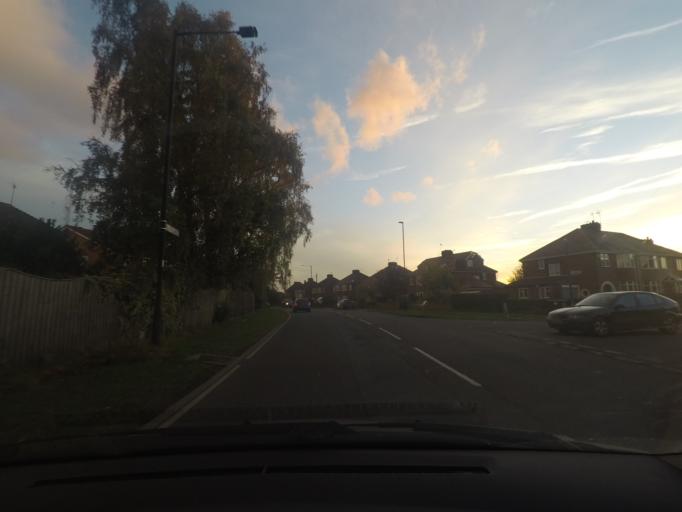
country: GB
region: England
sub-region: City of York
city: York
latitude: 53.9782
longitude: -1.0971
